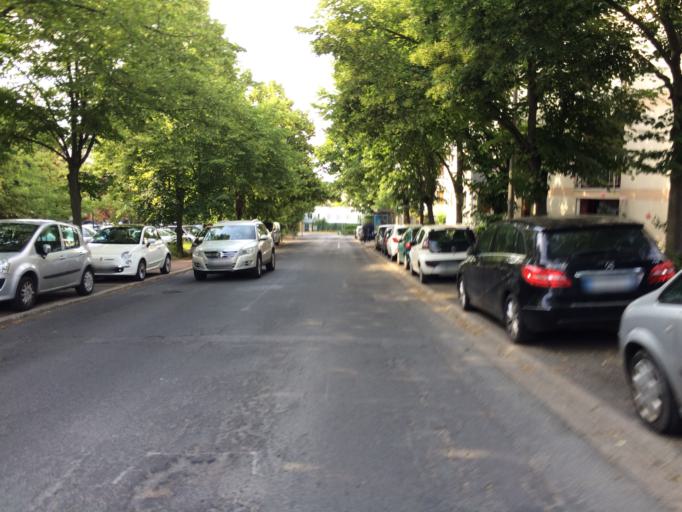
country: FR
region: Ile-de-France
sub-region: Departement de l'Essonne
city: Longjumeau
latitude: 48.6894
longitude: 2.2955
